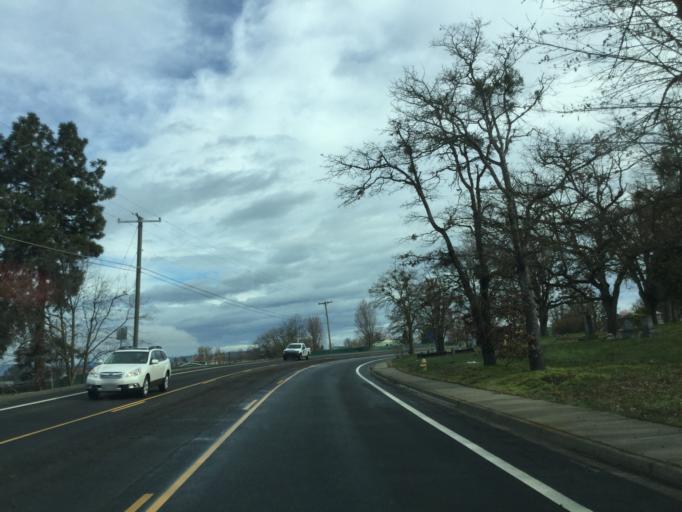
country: US
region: Oregon
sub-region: Jackson County
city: Central Point
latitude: 42.3857
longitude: -122.8930
